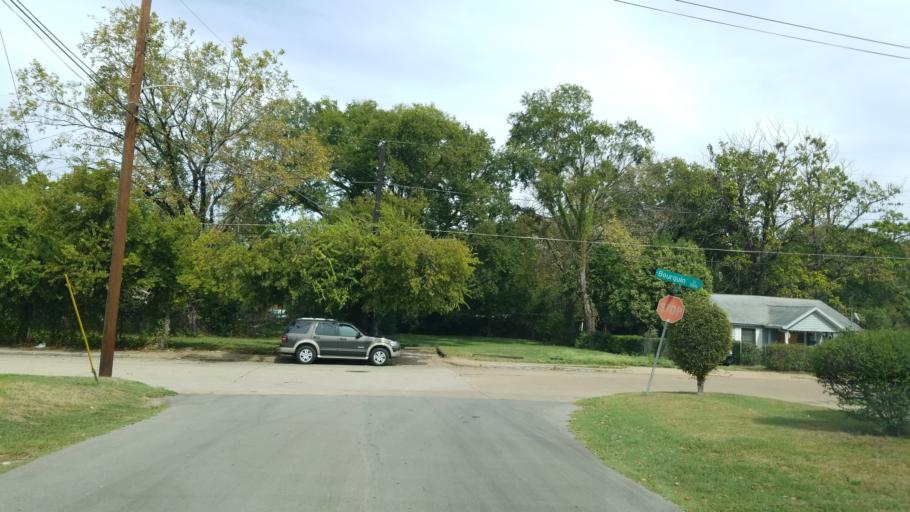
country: US
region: Texas
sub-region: Dallas County
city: Dallas
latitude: 32.7650
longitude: -96.7370
